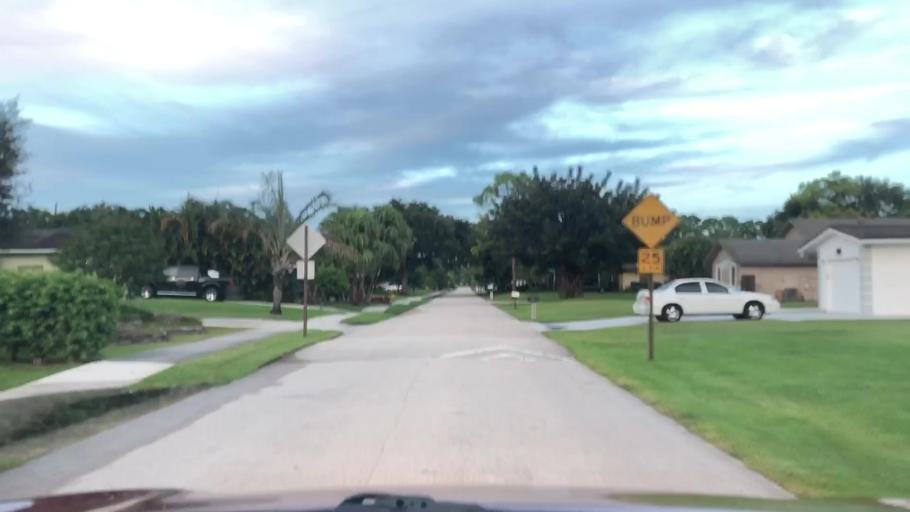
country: US
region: Florida
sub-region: Palm Beach County
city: Seminole Manor
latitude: 26.5639
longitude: -80.1222
